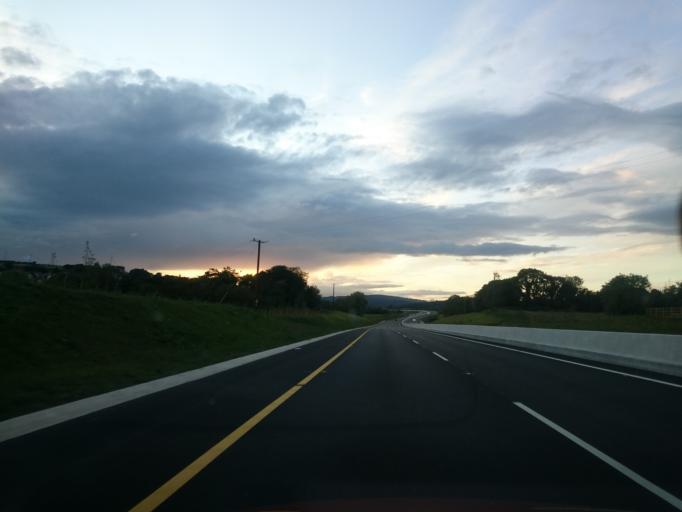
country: IE
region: Leinster
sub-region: Wicklow
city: Rathnew
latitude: 52.9079
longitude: -6.1049
